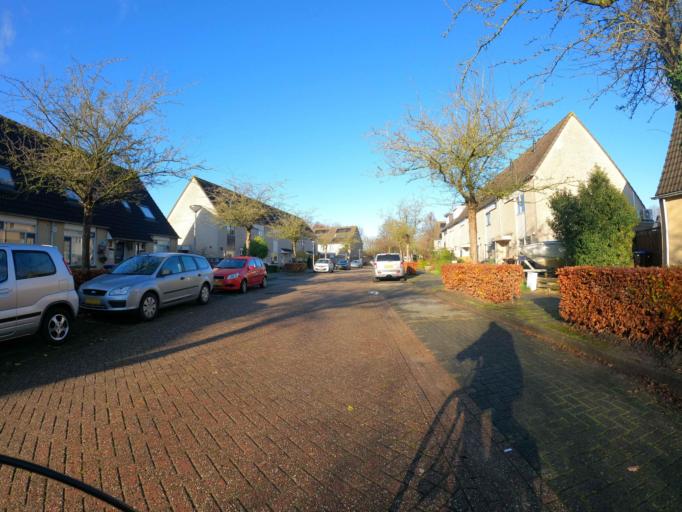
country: NL
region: Flevoland
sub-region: Gemeente Zeewolde
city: Zeewolde
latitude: 52.3220
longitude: 5.5360
